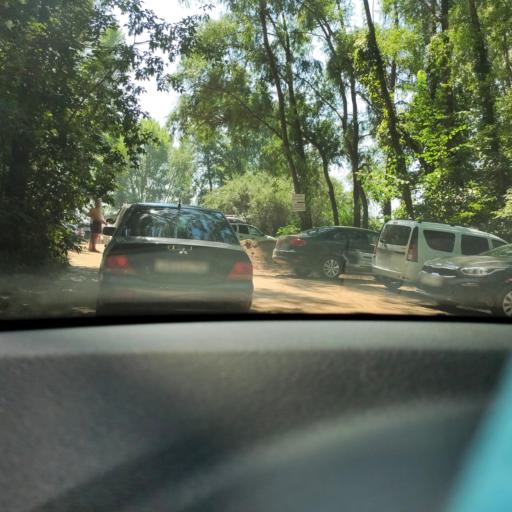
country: RU
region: Samara
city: Smyshlyayevka
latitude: 53.2197
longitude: 50.3438
